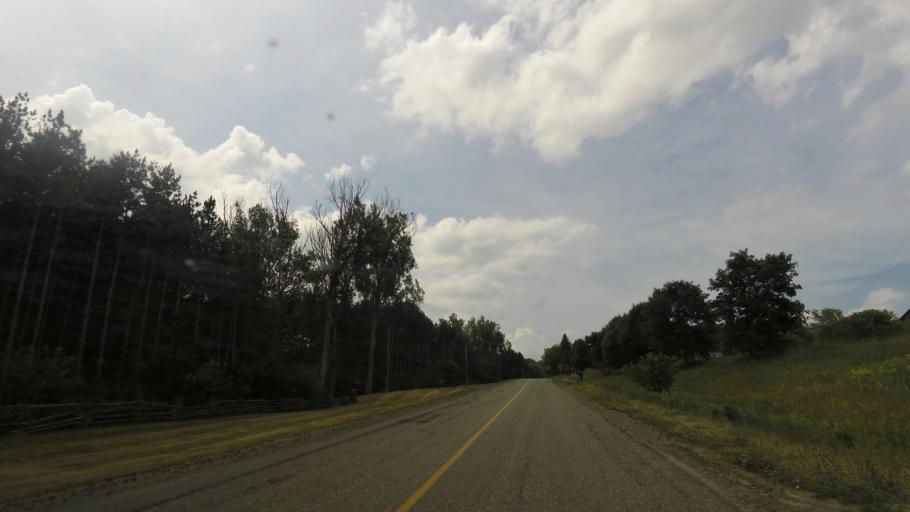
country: CA
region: Ontario
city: Orangeville
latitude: 43.8658
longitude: -79.9076
